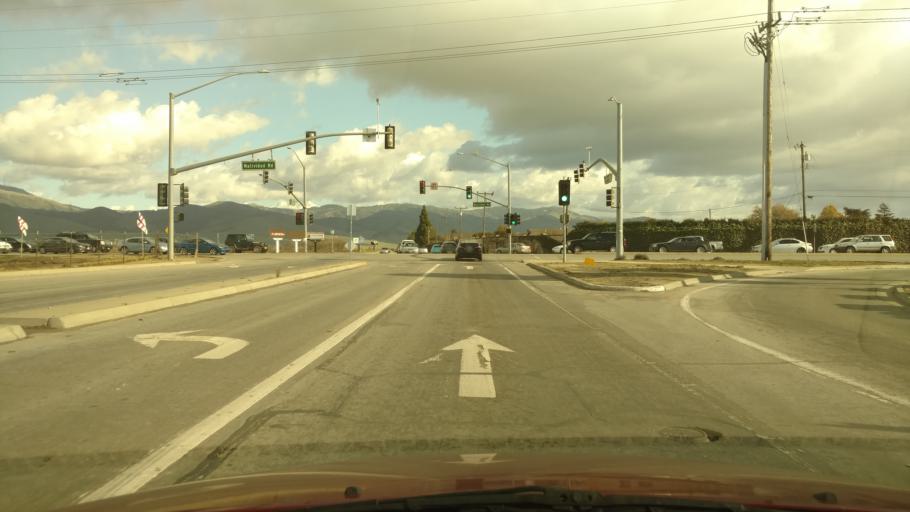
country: US
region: California
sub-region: Monterey County
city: Salinas
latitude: 36.7156
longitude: -121.6243
